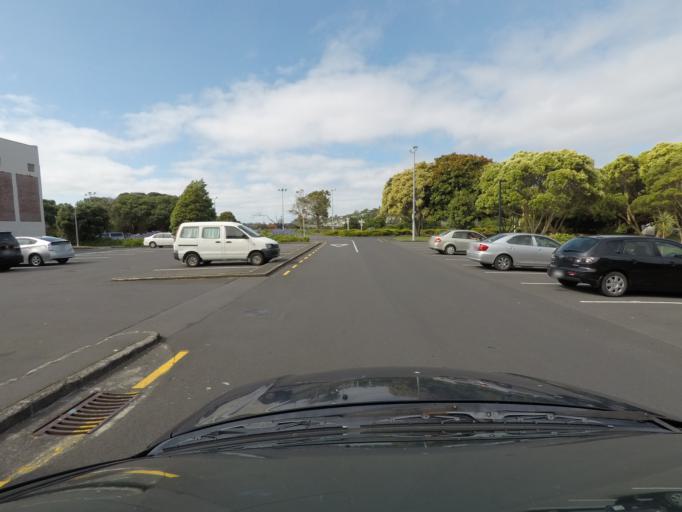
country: NZ
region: Auckland
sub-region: Auckland
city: Auckland
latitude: -36.9082
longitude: 174.7561
